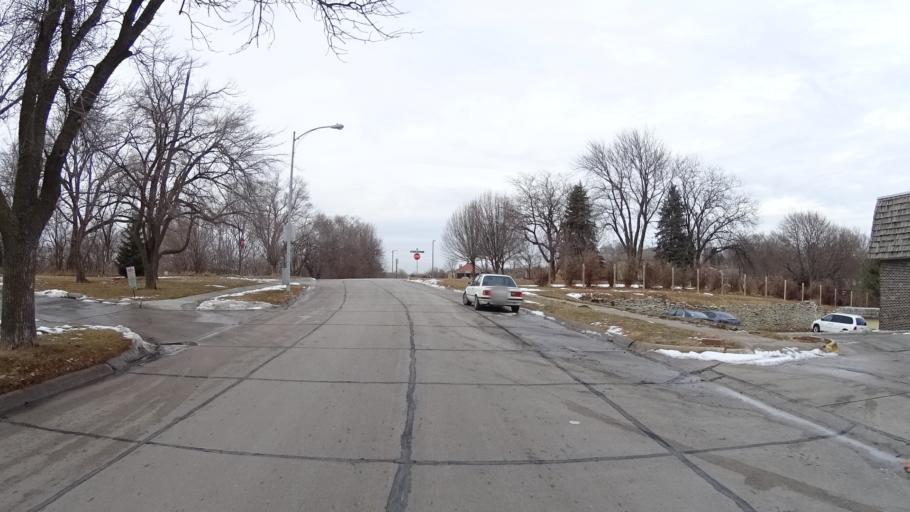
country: US
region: Nebraska
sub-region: Sarpy County
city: Bellevue
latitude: 41.1577
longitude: -95.9209
